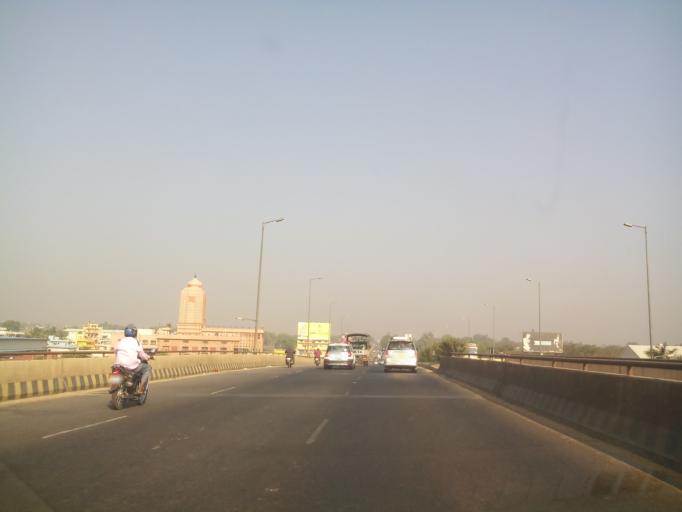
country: IN
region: Karnataka
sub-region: Bangalore Rural
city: Nelamangala
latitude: 13.0688
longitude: 77.4478
